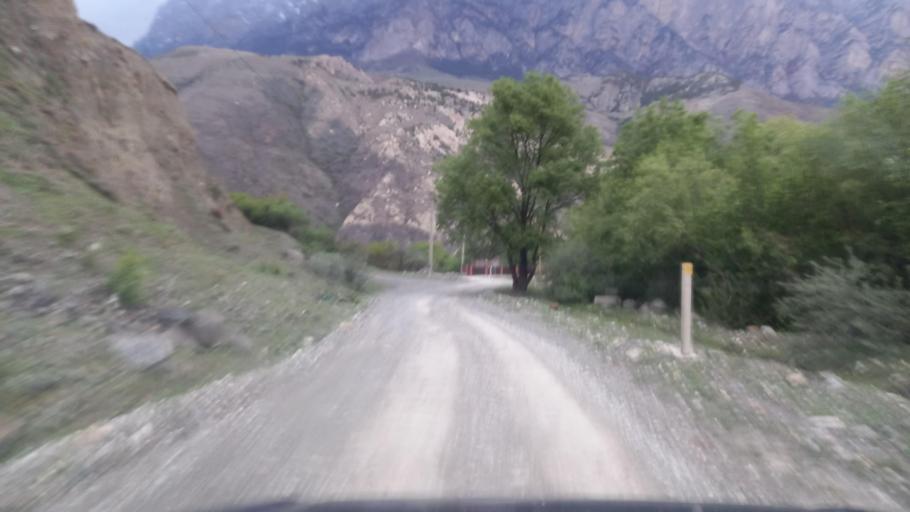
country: RU
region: North Ossetia
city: Mizur
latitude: 42.8580
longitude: 44.1486
